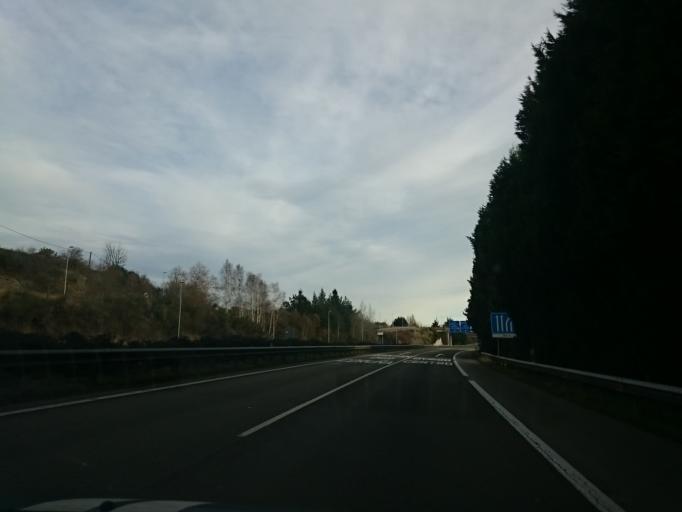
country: ES
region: Asturias
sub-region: Province of Asturias
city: Oviedo
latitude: 43.3406
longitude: -5.8682
